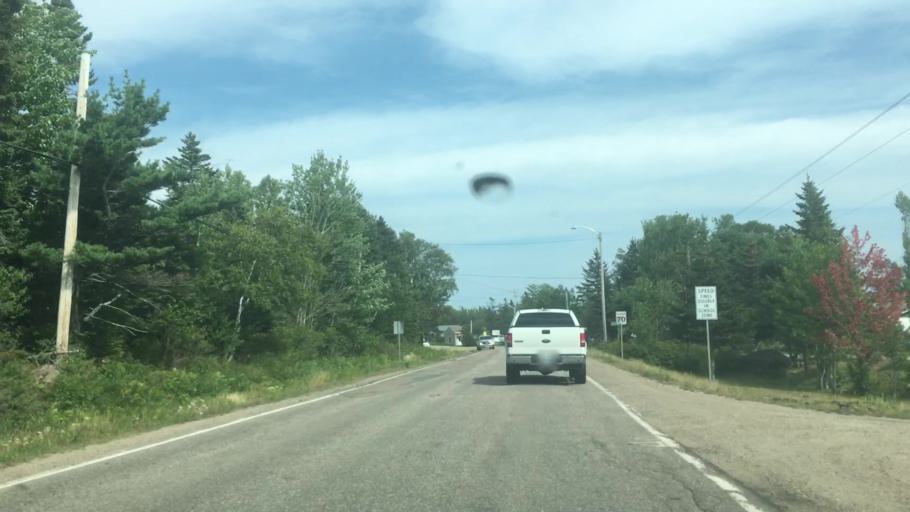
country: CA
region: Nova Scotia
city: Sydney Mines
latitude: 46.6901
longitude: -60.3839
